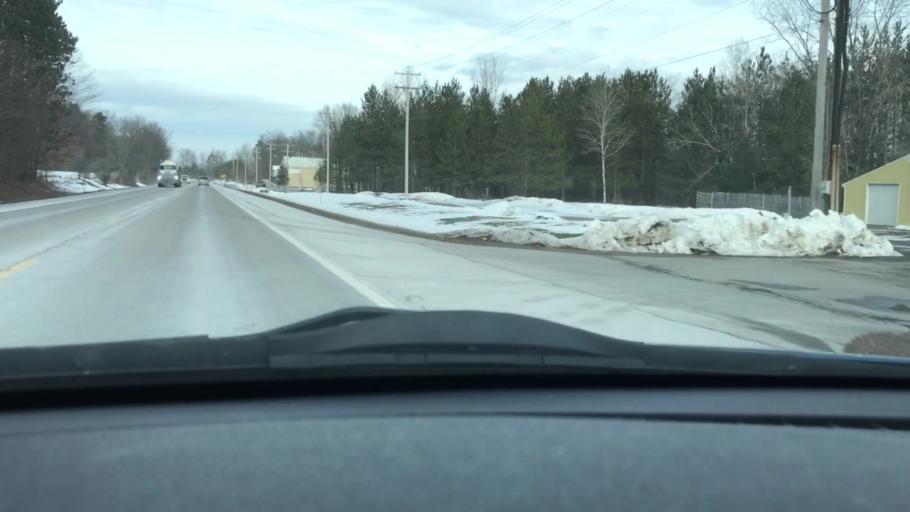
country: US
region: New York
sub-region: Oneida County
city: Boonville
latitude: 43.4935
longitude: -75.3292
